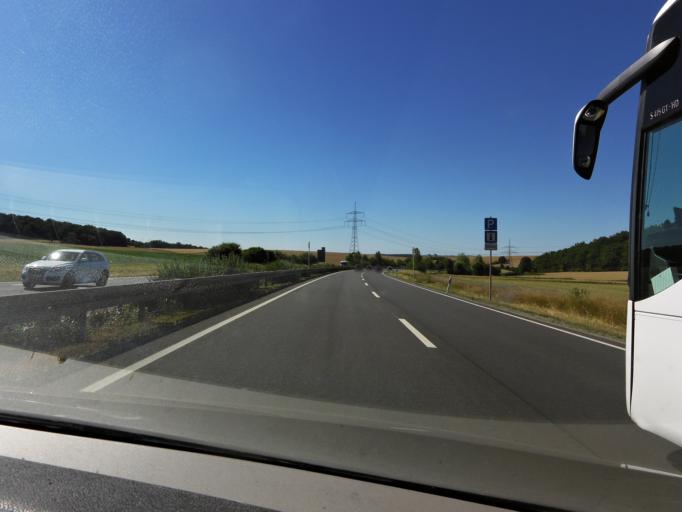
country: DE
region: Bavaria
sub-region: Regierungsbezirk Unterfranken
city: Biebelried
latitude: 49.7764
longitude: 10.0558
